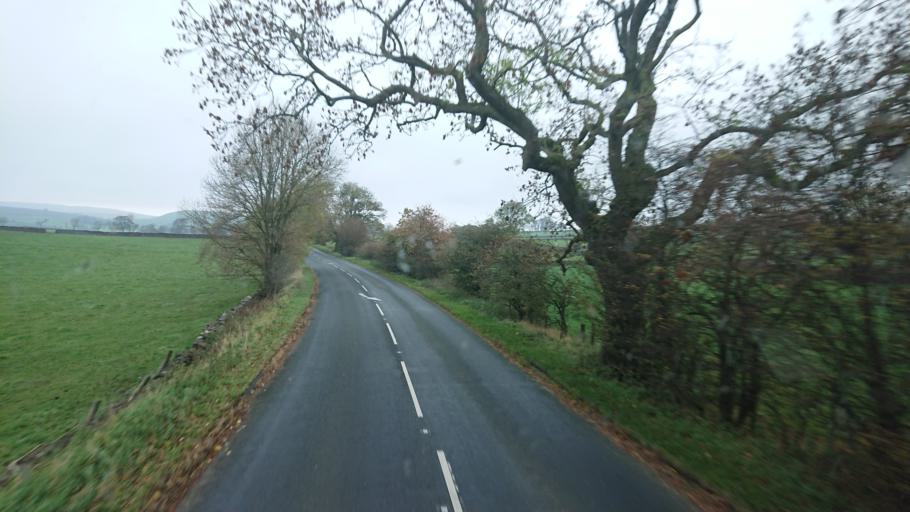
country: GB
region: England
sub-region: North Yorkshire
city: Skipton
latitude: 54.0278
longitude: -2.0446
